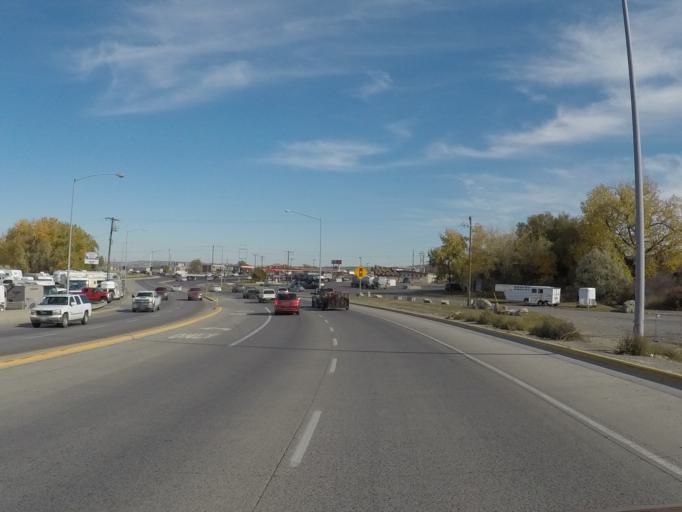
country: US
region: Montana
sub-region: Yellowstone County
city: Billings
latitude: 45.7960
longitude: -108.4638
